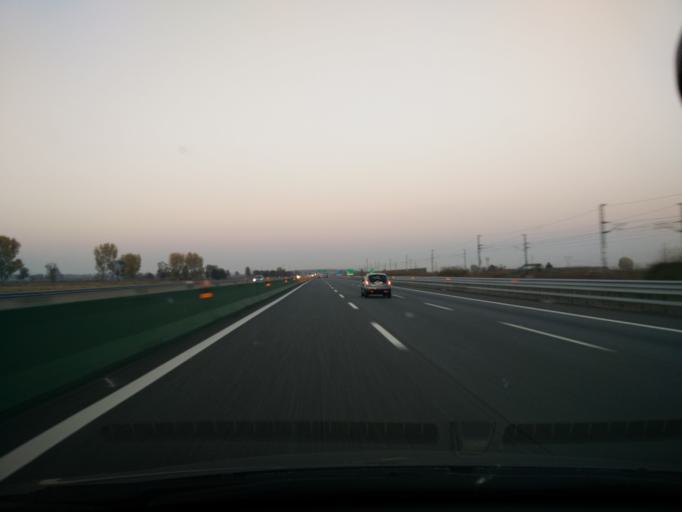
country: IT
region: Piedmont
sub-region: Provincia di Vercelli
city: Livorno Ferraris
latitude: 45.3112
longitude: 8.0620
